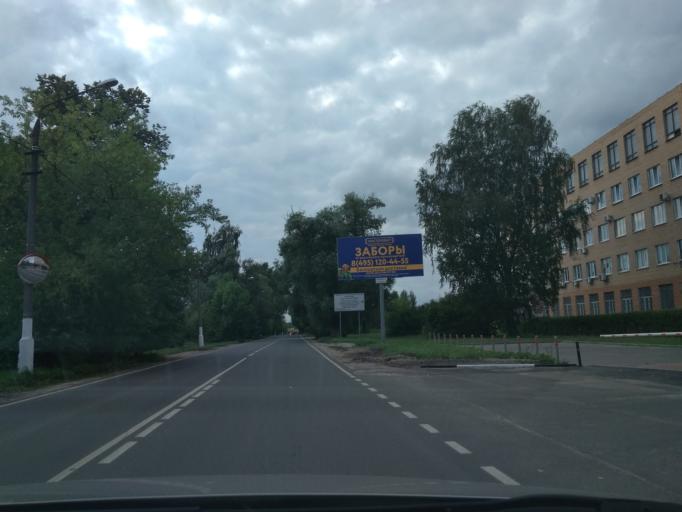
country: RU
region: Moskovskaya
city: Orekhovo-Zuyevo
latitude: 55.7962
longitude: 38.9411
